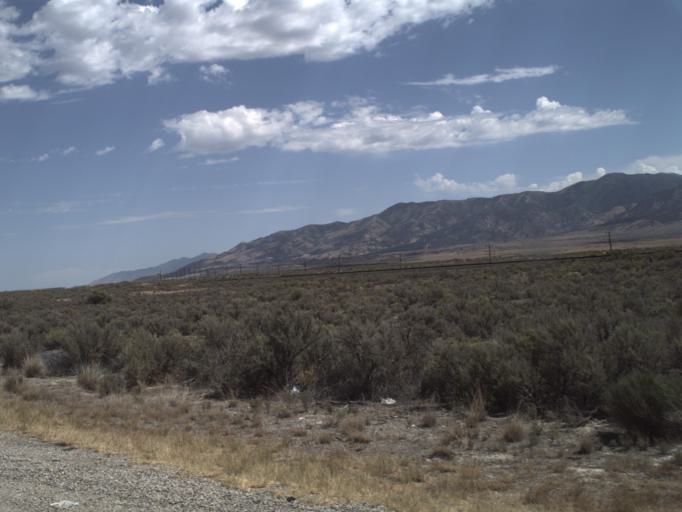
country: US
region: Utah
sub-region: Tooele County
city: Tooele
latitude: 40.3576
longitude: -112.4135
